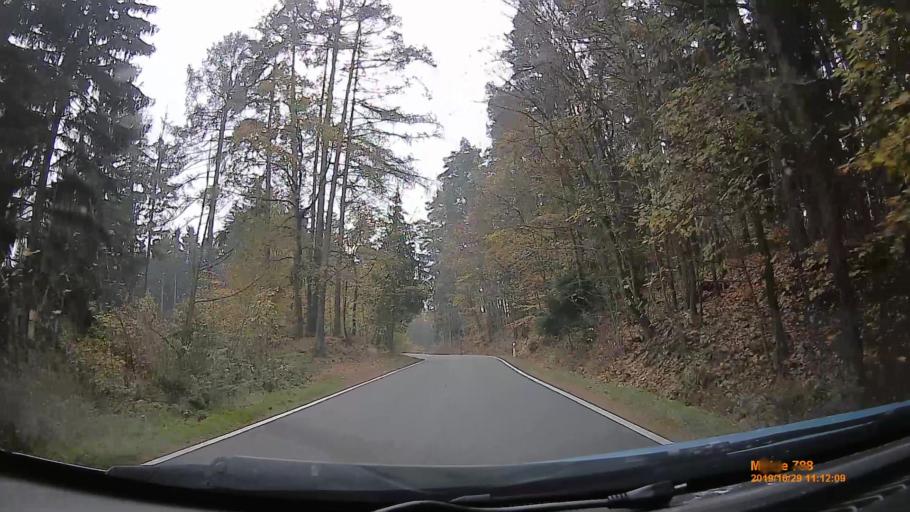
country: PL
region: Lower Silesian Voivodeship
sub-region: Powiat klodzki
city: Polanica-Zdroj
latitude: 50.4294
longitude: 16.5050
